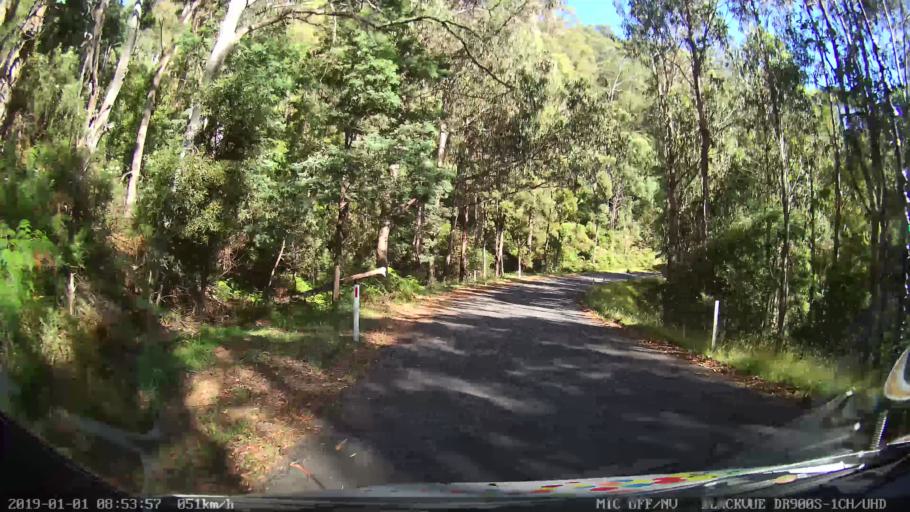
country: AU
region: New South Wales
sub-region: Snowy River
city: Jindabyne
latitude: -36.2625
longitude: 148.1896
